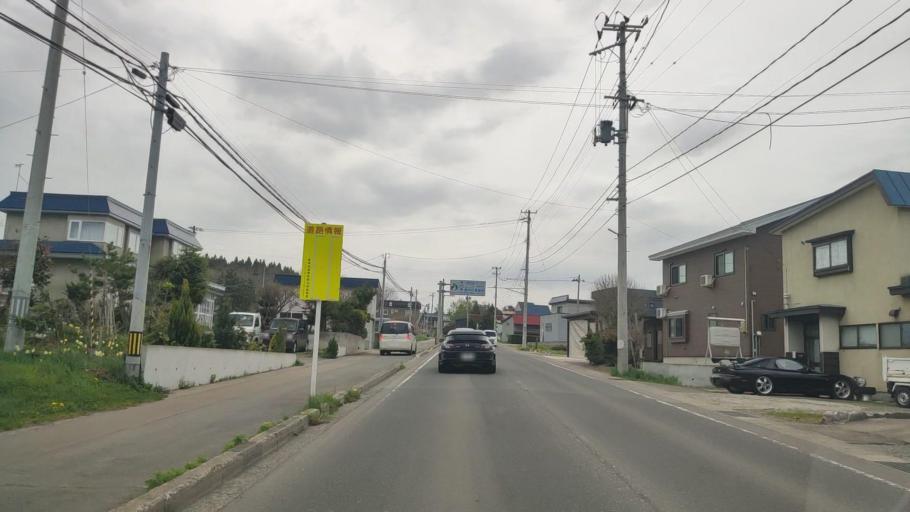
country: JP
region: Aomori
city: Aomori Shi
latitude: 40.7888
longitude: 140.7875
